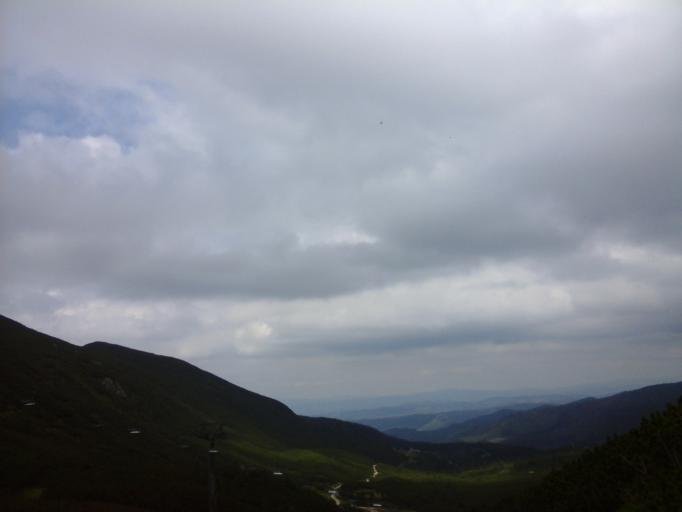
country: PL
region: Lesser Poland Voivodeship
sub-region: Powiat tatrzanski
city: Zakopane
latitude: 49.2348
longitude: 19.9943
